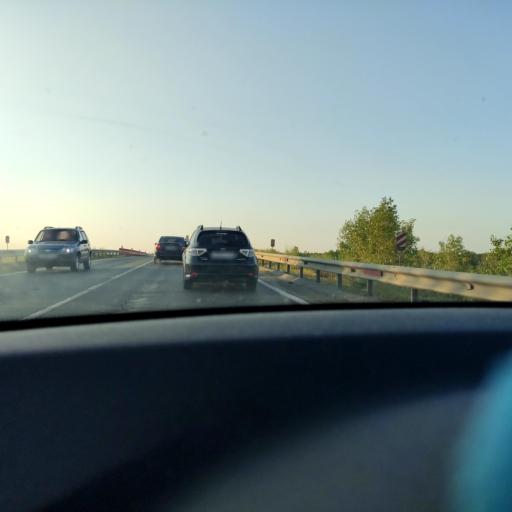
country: RU
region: Samara
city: Kinel'
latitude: 53.2507
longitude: 50.5915
